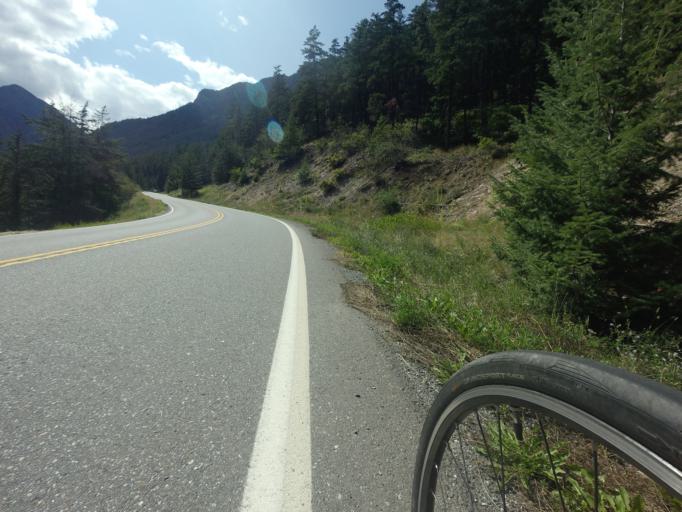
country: CA
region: British Columbia
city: Lillooet
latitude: 50.6533
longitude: -122.0052
